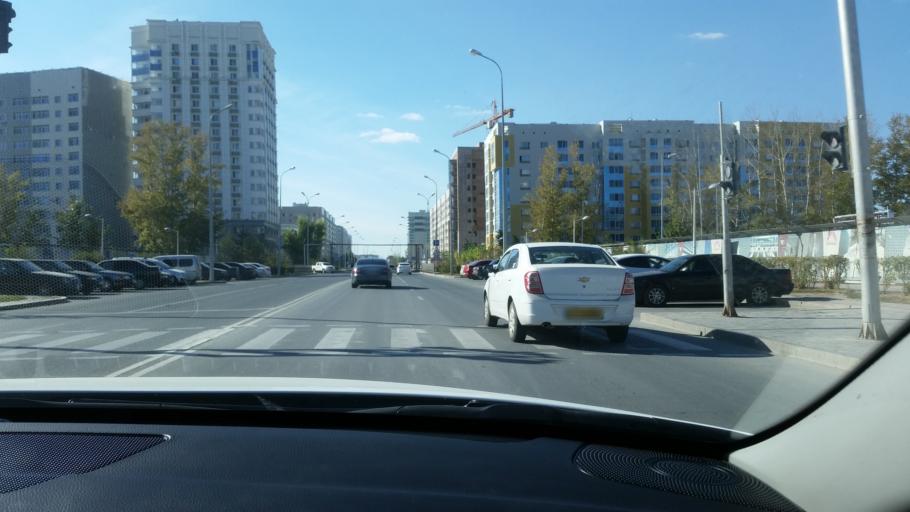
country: KZ
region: Astana Qalasy
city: Astana
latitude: 51.1164
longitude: 71.4259
